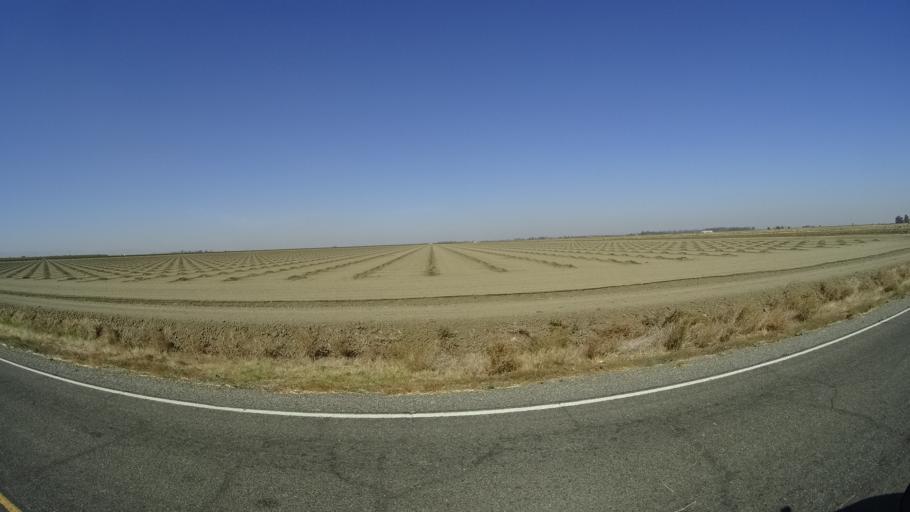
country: US
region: California
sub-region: Yolo County
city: Winters
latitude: 38.5907
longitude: -121.8968
